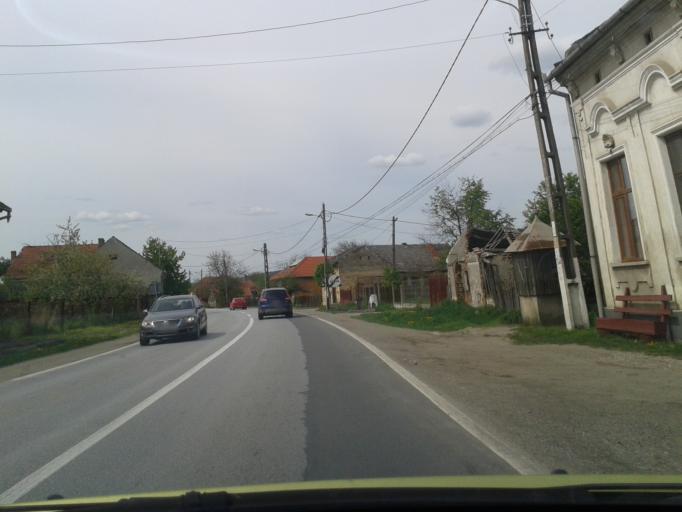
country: RO
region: Hunedoara
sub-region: Comuna Dobra
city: Dobra
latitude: 45.9147
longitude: 22.5644
